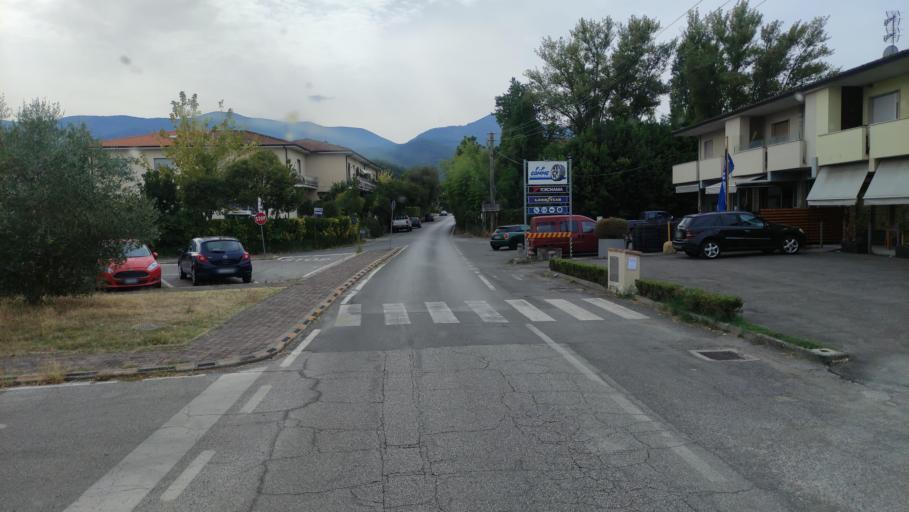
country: IT
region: Tuscany
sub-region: Provincia di Lucca
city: Lucca
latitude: 43.8107
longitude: 10.4988
